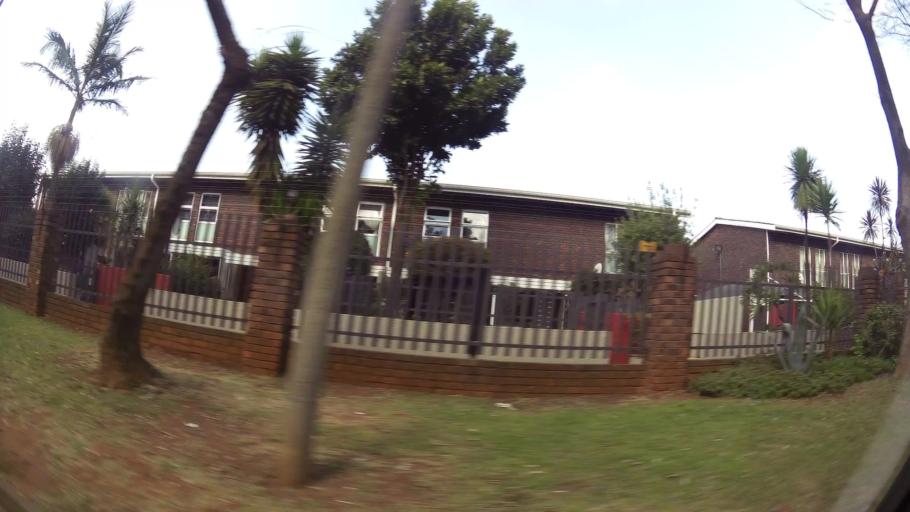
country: ZA
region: Gauteng
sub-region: Ekurhuleni Metropolitan Municipality
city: Boksburg
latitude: -26.1886
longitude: 28.2311
